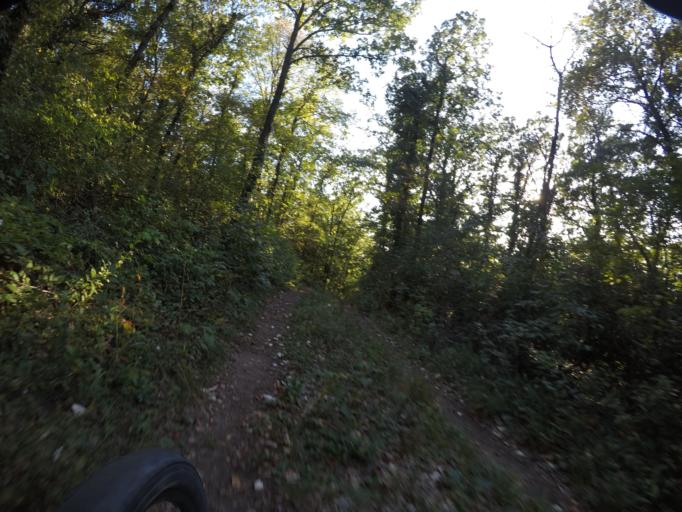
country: AT
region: Lower Austria
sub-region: Politischer Bezirk Bruck an der Leitha
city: Mannersdorf am Leithagebirge
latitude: 47.9653
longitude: 16.6015
